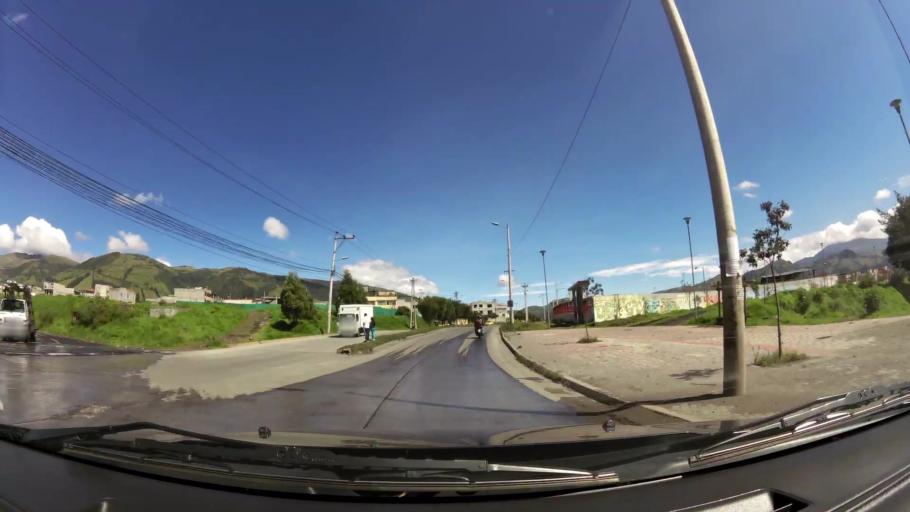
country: EC
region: Pichincha
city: Quito
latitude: -0.3025
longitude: -78.5537
